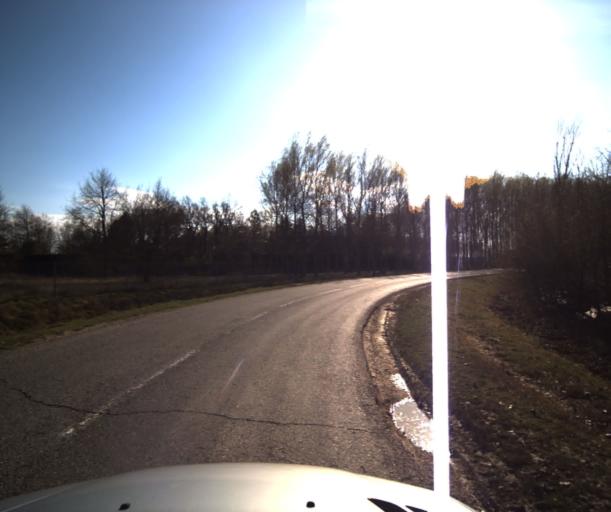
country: FR
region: Midi-Pyrenees
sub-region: Departement du Tarn-et-Garonne
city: Campsas
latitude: 43.9280
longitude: 1.3165
